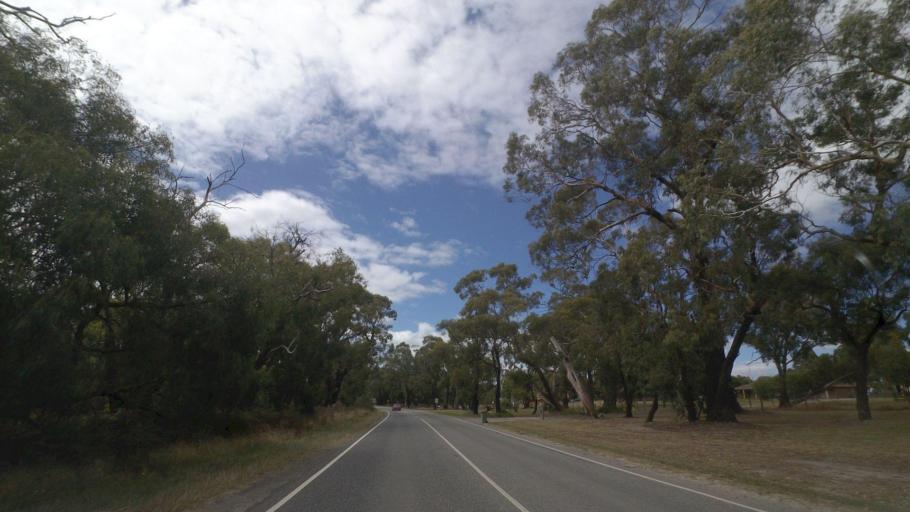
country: AU
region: Victoria
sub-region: Cardinia
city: Koo-Wee-Rup
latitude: -38.2728
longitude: 145.5705
